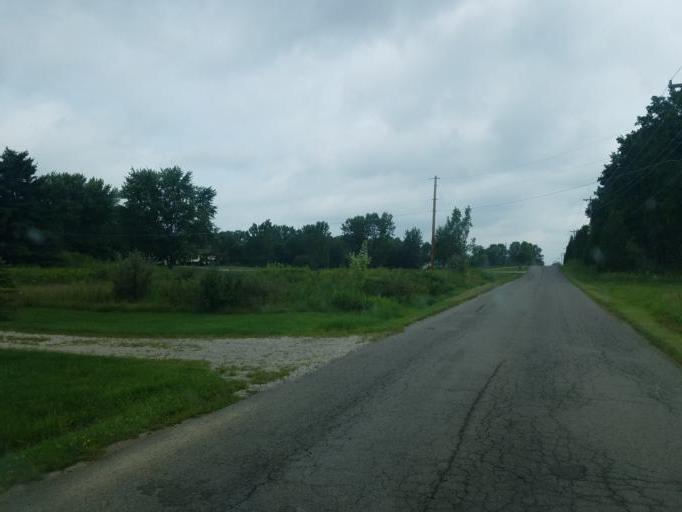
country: US
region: Ohio
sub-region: Morrow County
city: Mount Gilead
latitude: 40.4804
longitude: -82.7816
